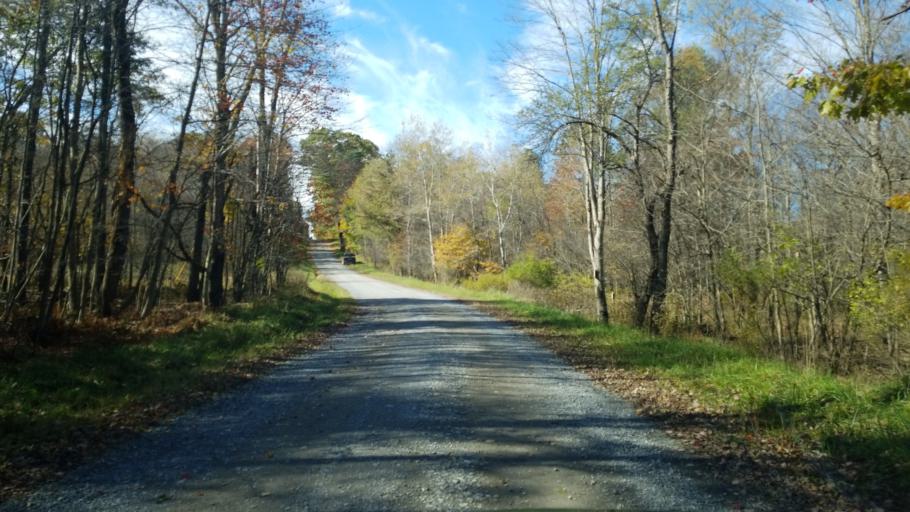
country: US
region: Pennsylvania
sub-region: Jefferson County
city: Falls Creek
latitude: 41.1916
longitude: -78.7828
